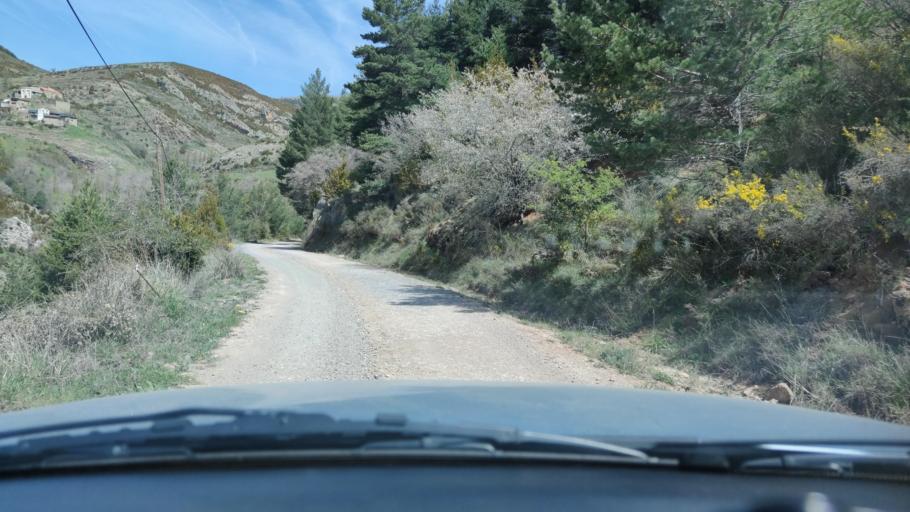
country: ES
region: Catalonia
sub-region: Provincia de Lleida
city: Sort
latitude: 42.2929
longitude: 1.1821
